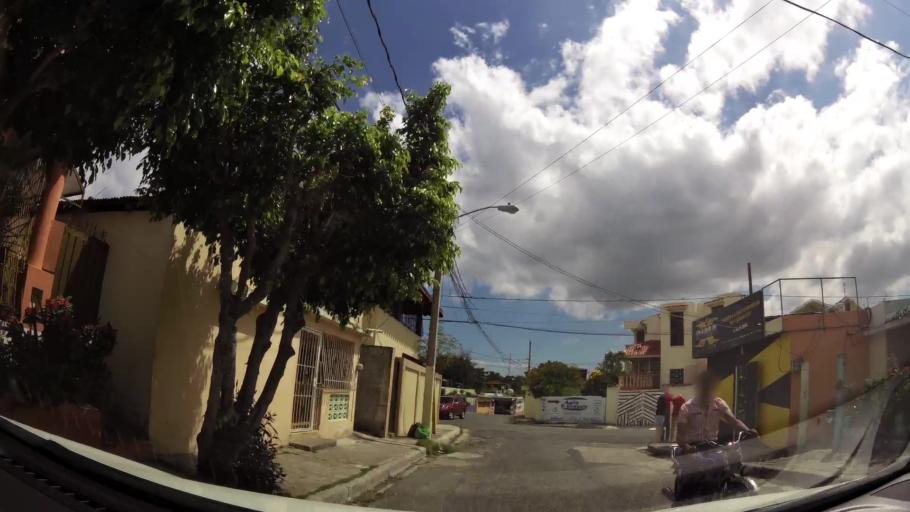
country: DO
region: San Cristobal
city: San Cristobal
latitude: 18.4136
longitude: -70.1165
